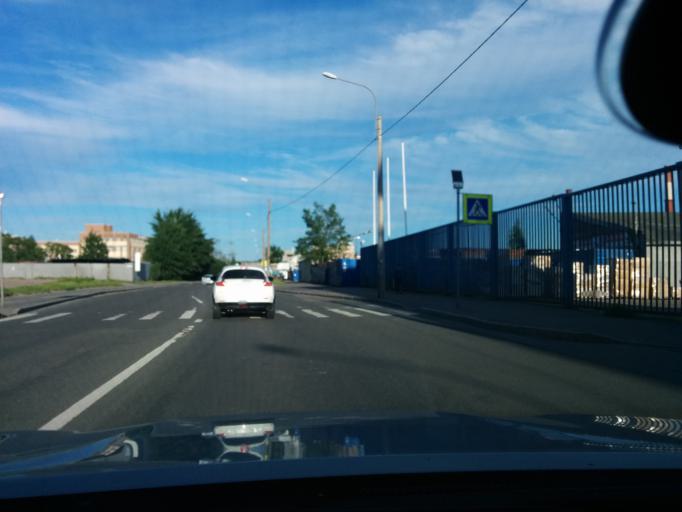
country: RU
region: Leningrad
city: Finlyandskiy
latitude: 59.9762
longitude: 30.3702
